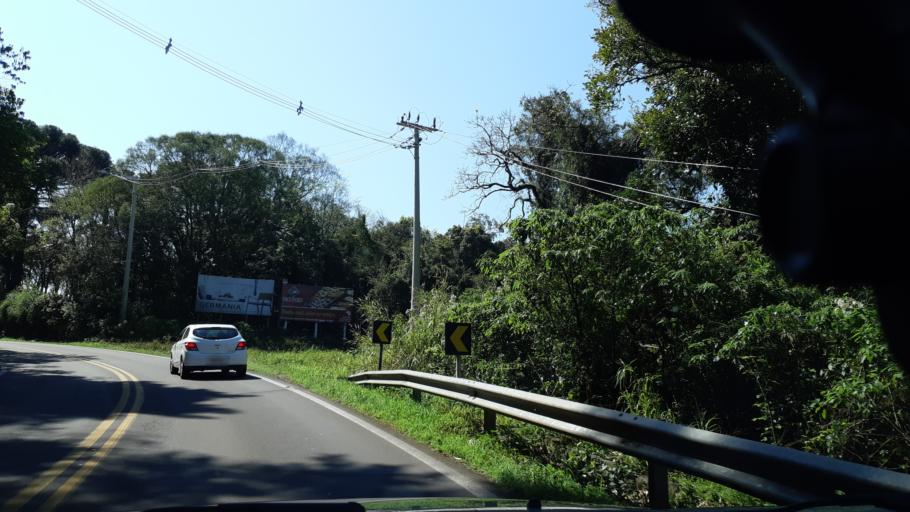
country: BR
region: Rio Grande do Sul
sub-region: Nova Petropolis
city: Nova Petropolis
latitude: -29.3960
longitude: -51.1248
